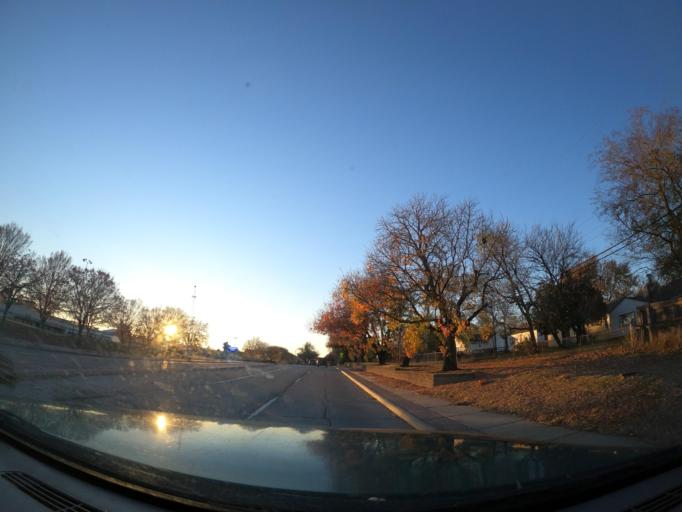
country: US
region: Oklahoma
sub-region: Tulsa County
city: Tulsa
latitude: 36.1406
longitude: -95.9272
